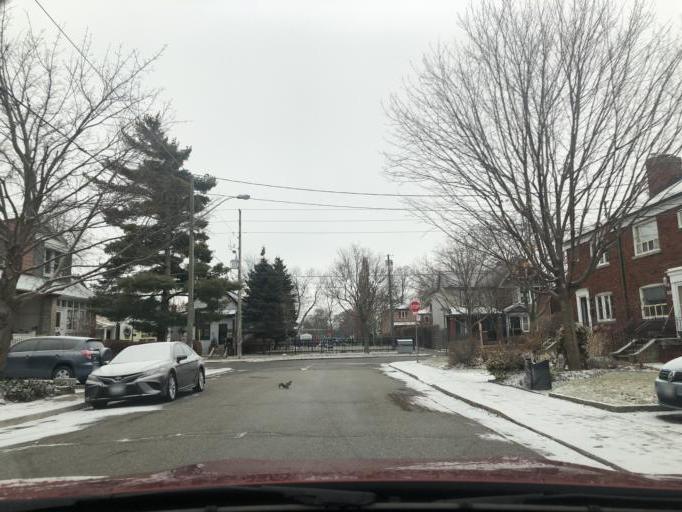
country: CA
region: Ontario
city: Toronto
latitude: 43.6860
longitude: -79.3416
